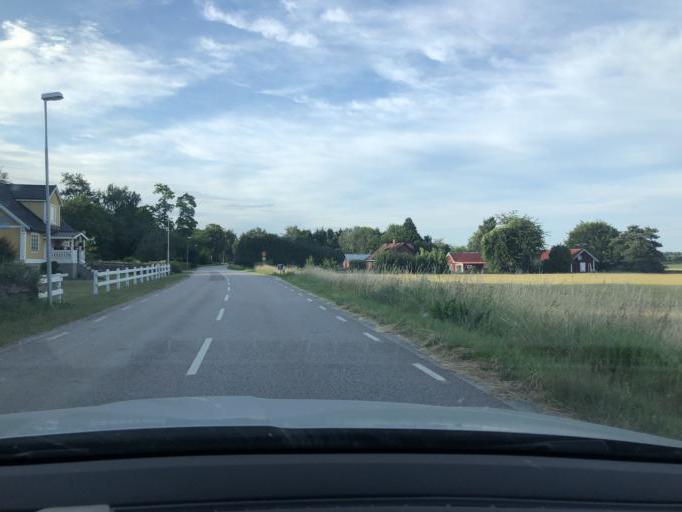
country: SE
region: Blekinge
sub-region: Solvesborgs Kommun
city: Soelvesborg
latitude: 56.1013
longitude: 14.6175
